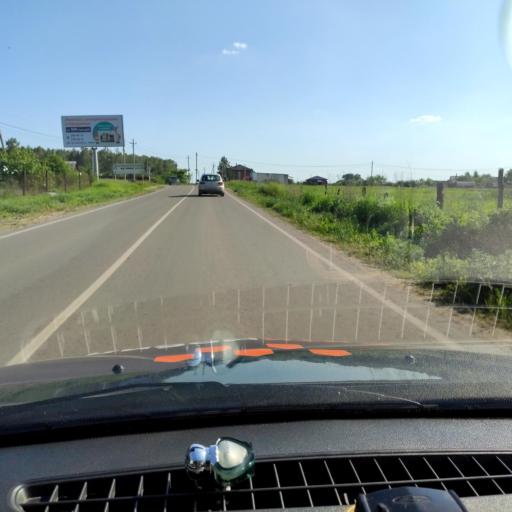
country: RU
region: Voronezj
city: Podgornoye
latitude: 51.8472
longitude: 39.1470
